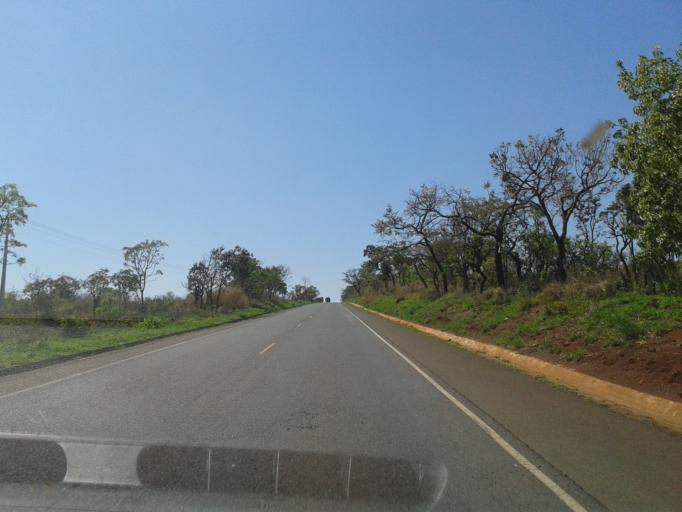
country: BR
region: Minas Gerais
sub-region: Uberlandia
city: Uberlandia
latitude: -19.1119
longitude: -47.9730
